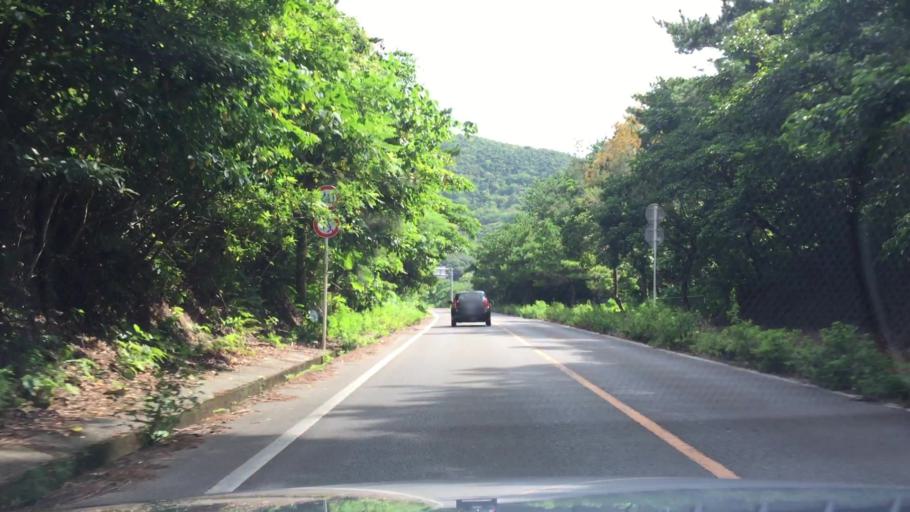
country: JP
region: Okinawa
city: Ishigaki
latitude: 24.4339
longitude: 124.2108
